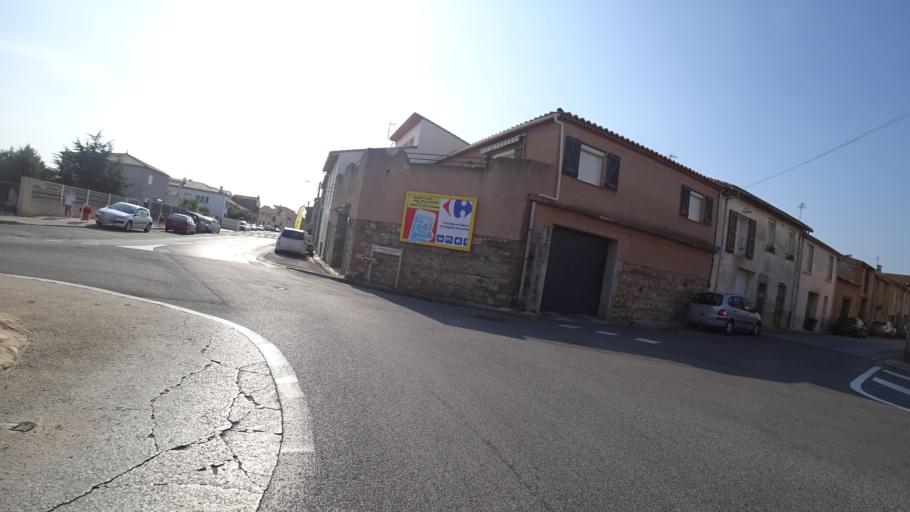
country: FR
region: Languedoc-Roussillon
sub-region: Departement des Pyrenees-Orientales
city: Claira
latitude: 42.7614
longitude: 2.9546
